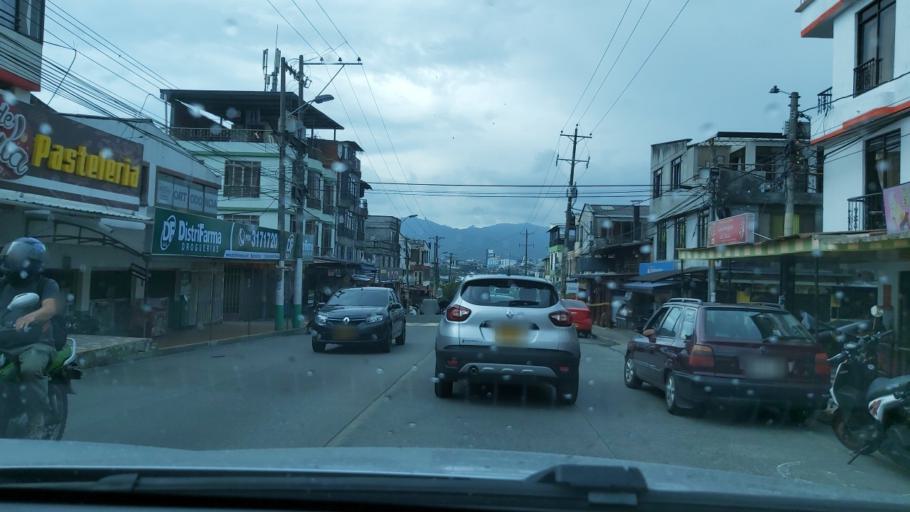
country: CO
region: Risaralda
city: Pereira
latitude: 4.7965
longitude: -75.7084
